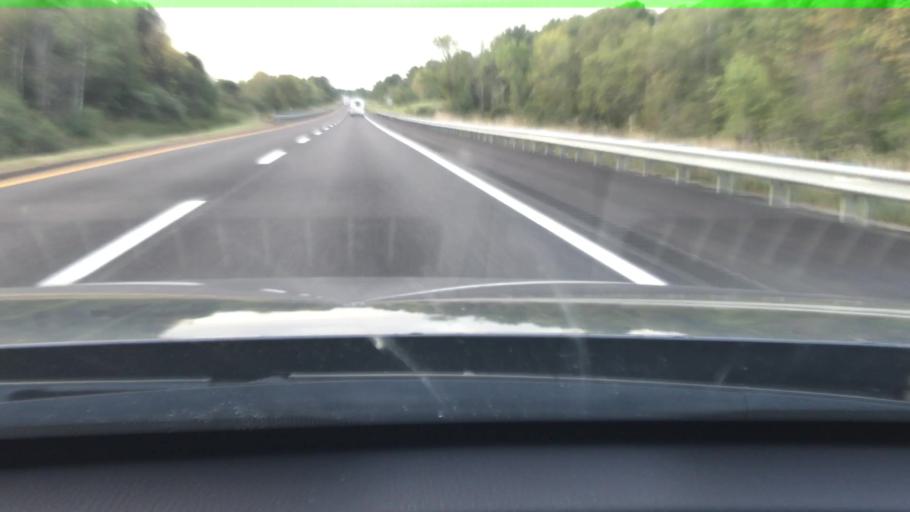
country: US
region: Maine
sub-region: Sagadahoc County
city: Richmond
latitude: 44.0753
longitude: -69.8796
